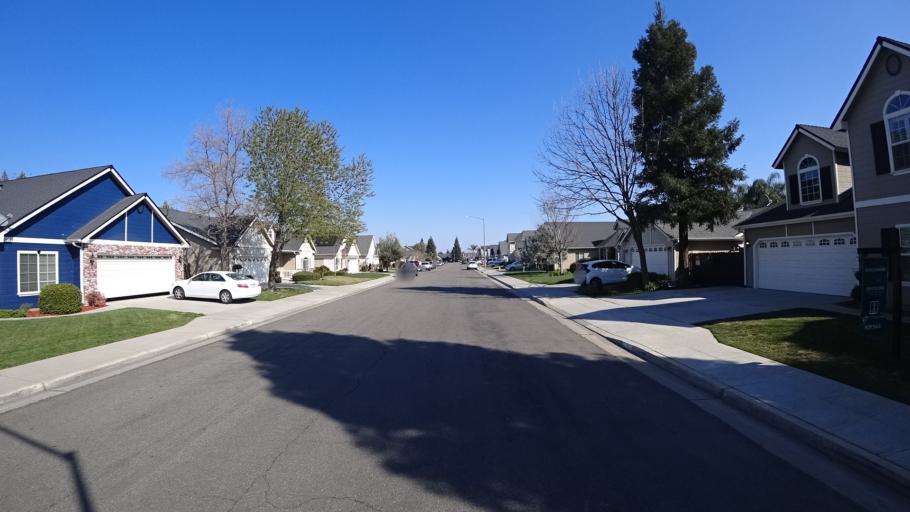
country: US
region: California
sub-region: Fresno County
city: Clovis
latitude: 36.8694
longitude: -119.7334
